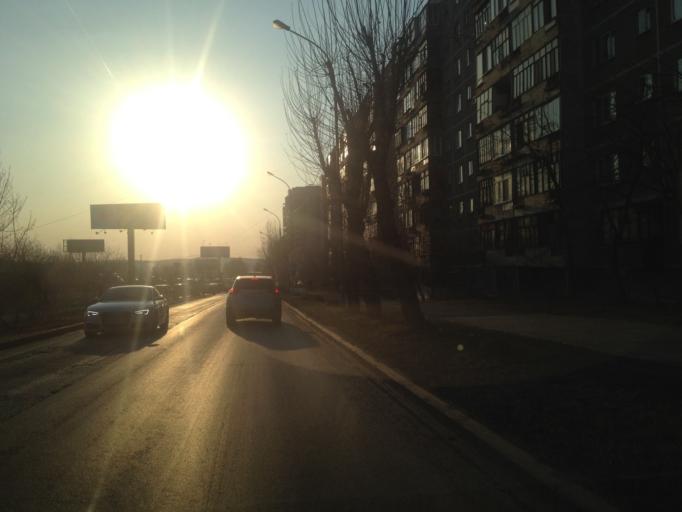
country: RU
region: Sverdlovsk
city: Sovkhoznyy
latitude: 56.8265
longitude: 60.5472
